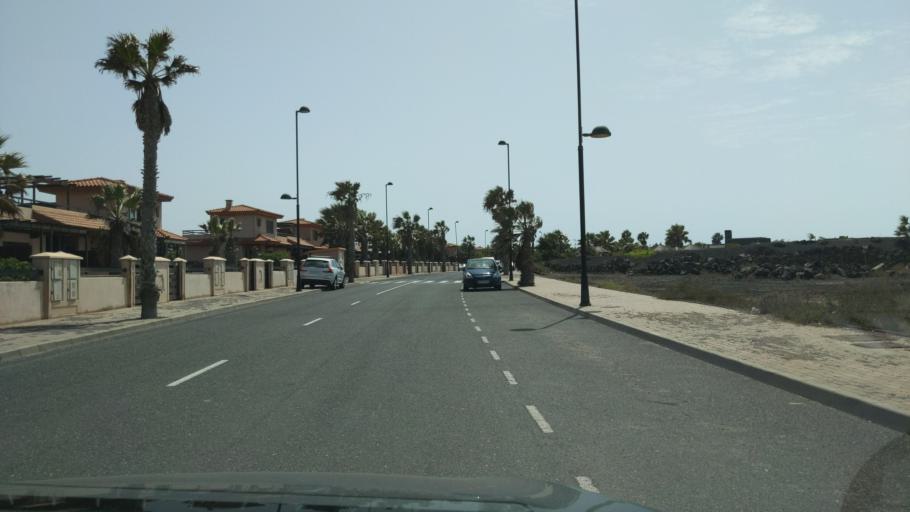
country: ES
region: Canary Islands
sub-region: Provincia de Las Palmas
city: Corralejo
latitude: 28.7318
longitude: -13.9464
